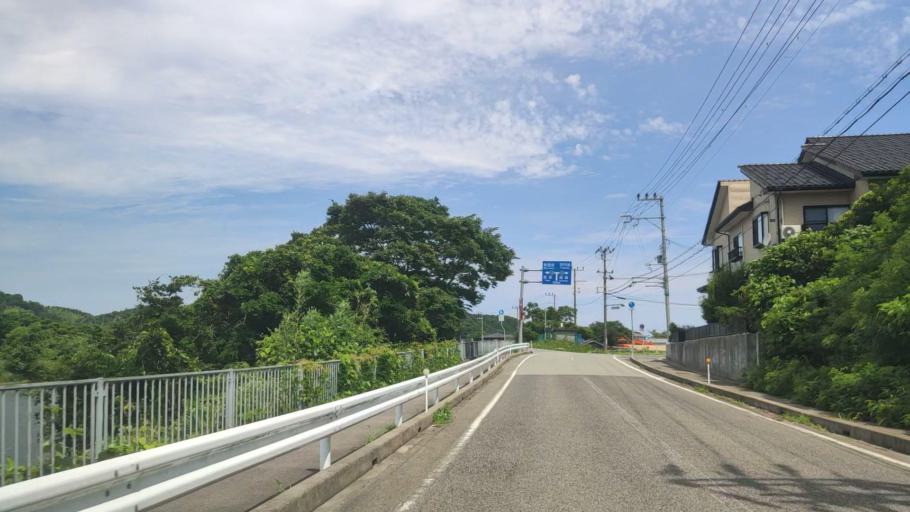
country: JP
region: Hyogo
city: Toyooka
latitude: 35.6524
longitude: 134.7630
